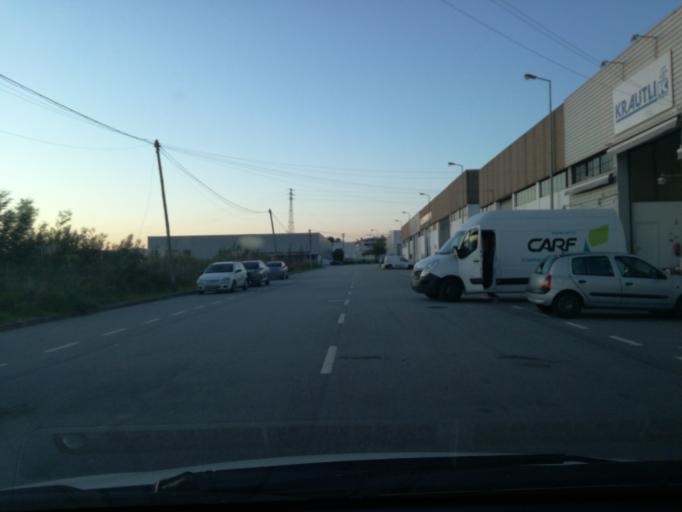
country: PT
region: Porto
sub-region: Maia
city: Gemunde
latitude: 41.2552
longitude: -8.6408
